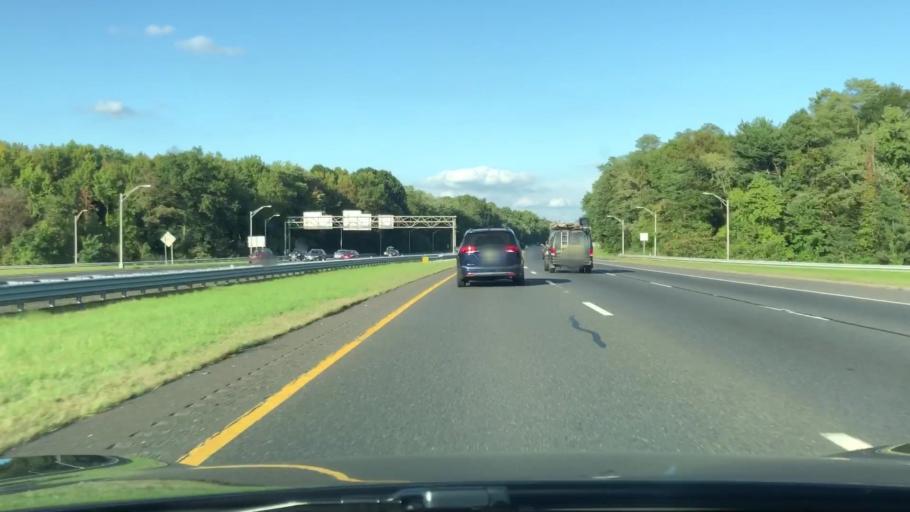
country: US
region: New Jersey
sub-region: Burlington County
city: Willingboro
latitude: 40.0456
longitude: -74.8333
